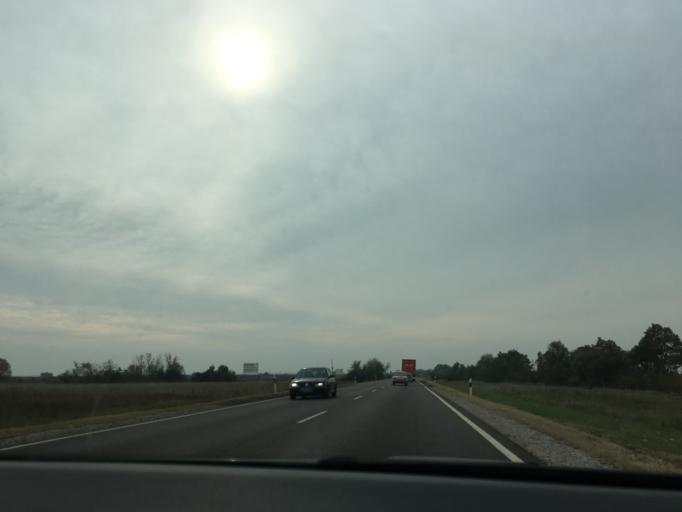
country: HU
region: Jasz-Nagykun-Szolnok
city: Kisujszallas
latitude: 47.2463
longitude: 20.8333
